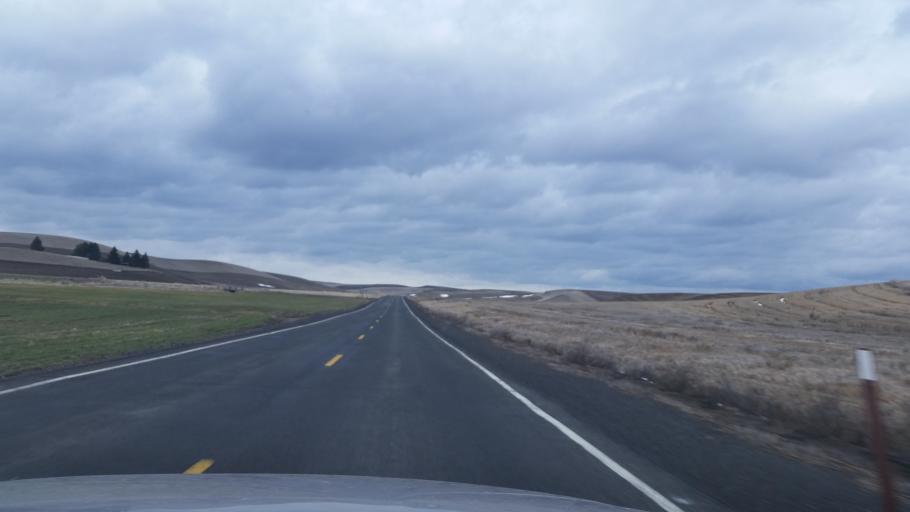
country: US
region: Washington
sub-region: Spokane County
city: Cheney
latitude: 47.1609
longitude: -117.8710
